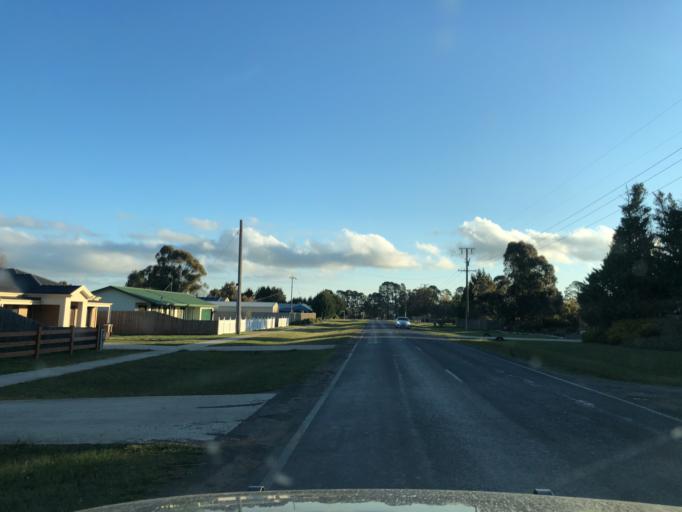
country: AU
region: Victoria
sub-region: Moorabool
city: Bacchus Marsh
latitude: -37.5936
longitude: 144.2339
